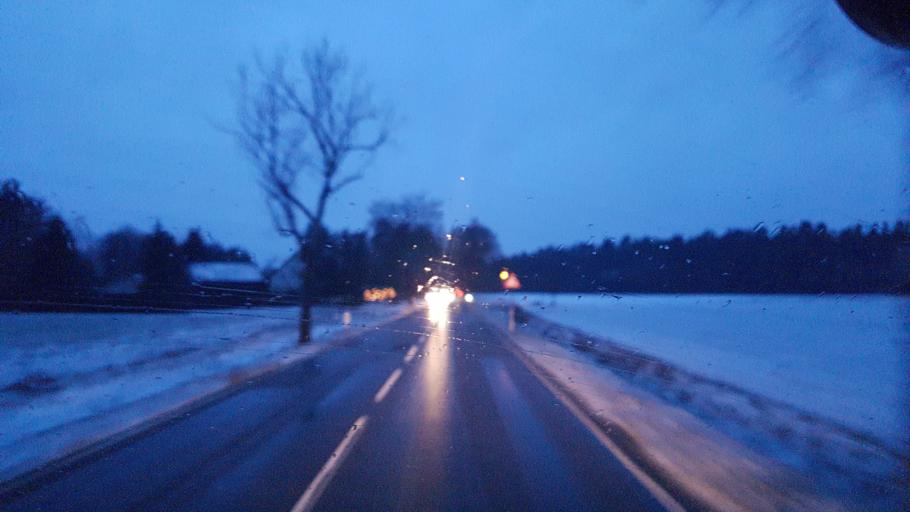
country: DE
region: Brandenburg
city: Briesen
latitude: 51.8059
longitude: 14.2446
